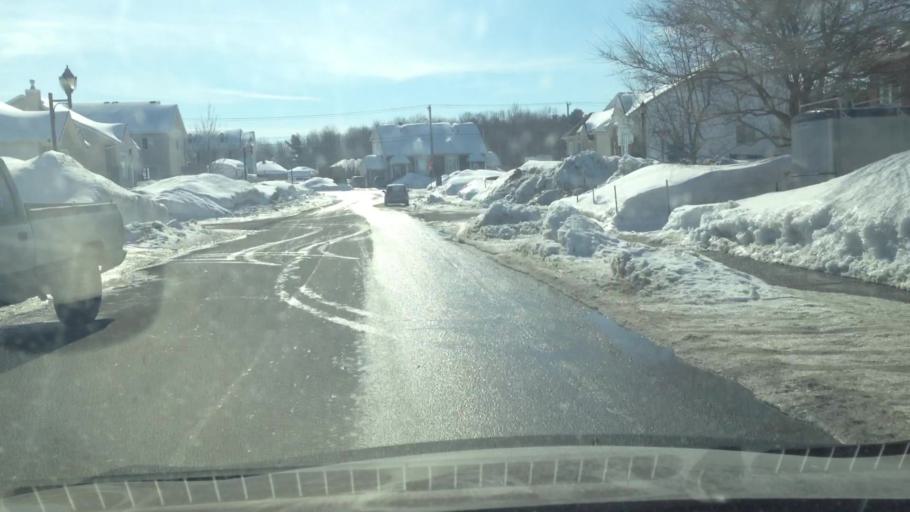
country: CA
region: Quebec
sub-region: Laurentides
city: Saint-Jerome
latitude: 45.7752
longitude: -73.9742
